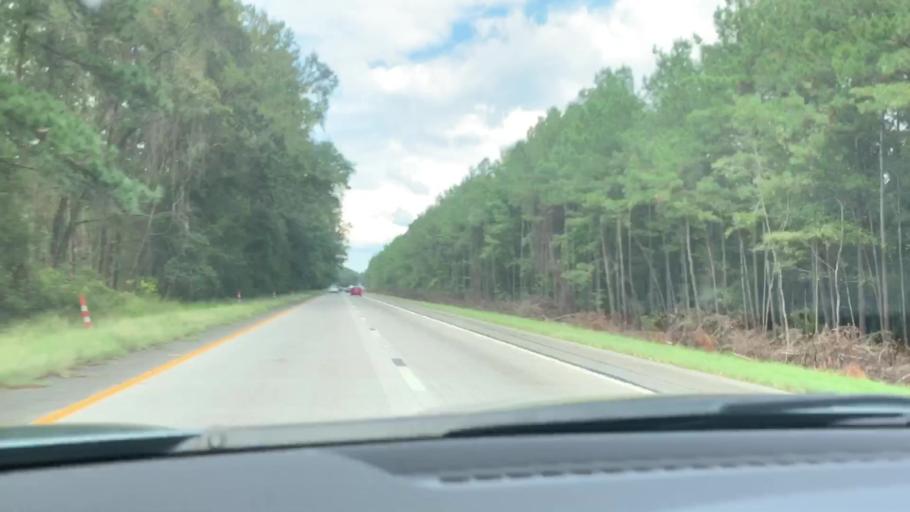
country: US
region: South Carolina
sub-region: Jasper County
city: Ridgeland
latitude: 32.4107
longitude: -81.0139
